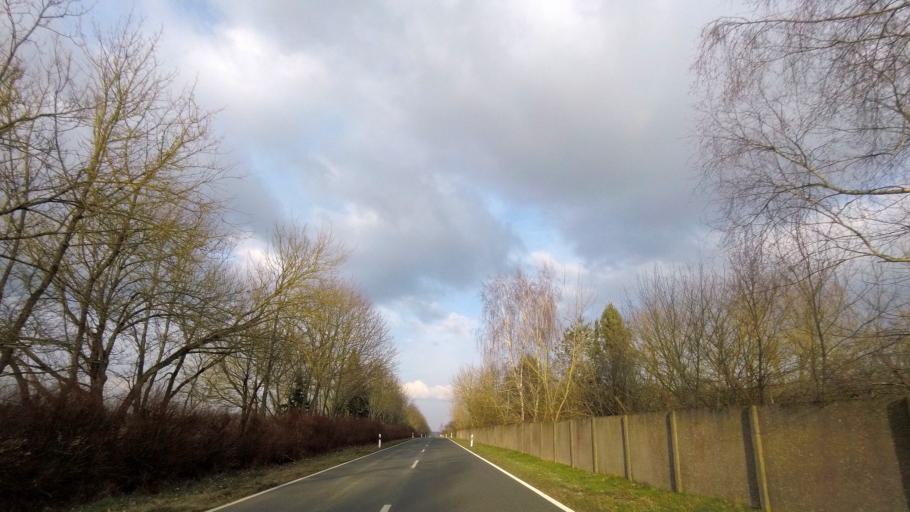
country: DE
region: Brandenburg
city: Belzig
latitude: 52.1177
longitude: 12.5789
